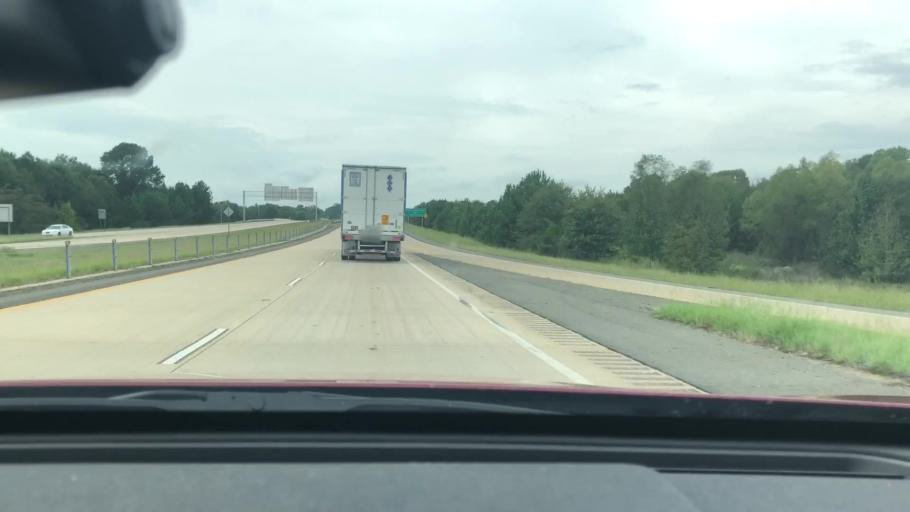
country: US
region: Texas
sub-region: Bowie County
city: Texarkana
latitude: 33.3871
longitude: -94.0232
